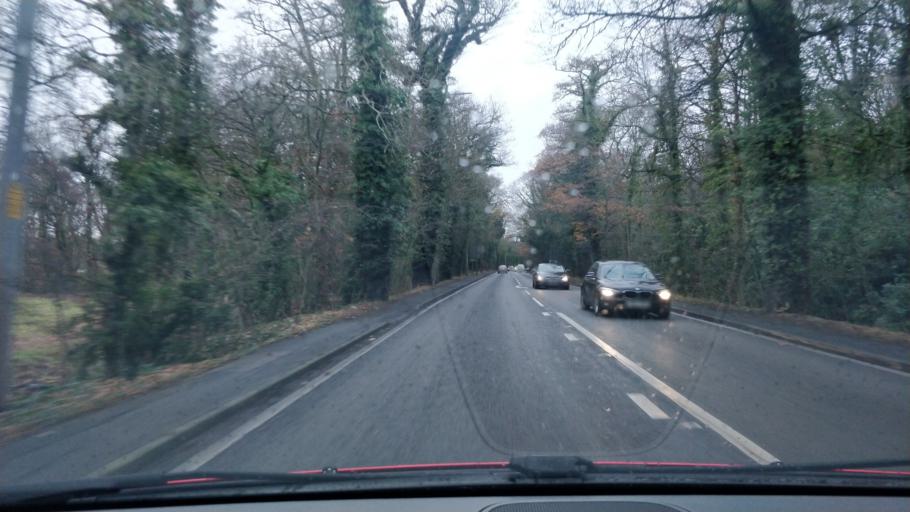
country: GB
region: England
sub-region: Sefton
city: Ince Blundell
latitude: 53.5165
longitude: -3.0197
